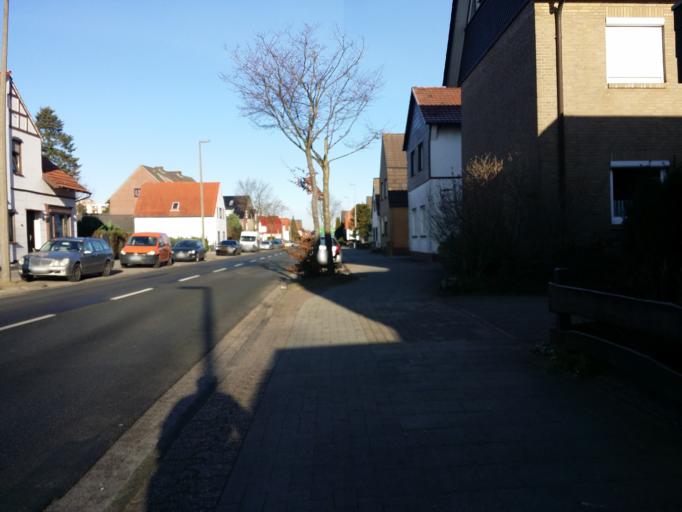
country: DE
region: Lower Saxony
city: Delmenhorst
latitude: 53.0465
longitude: 8.6565
